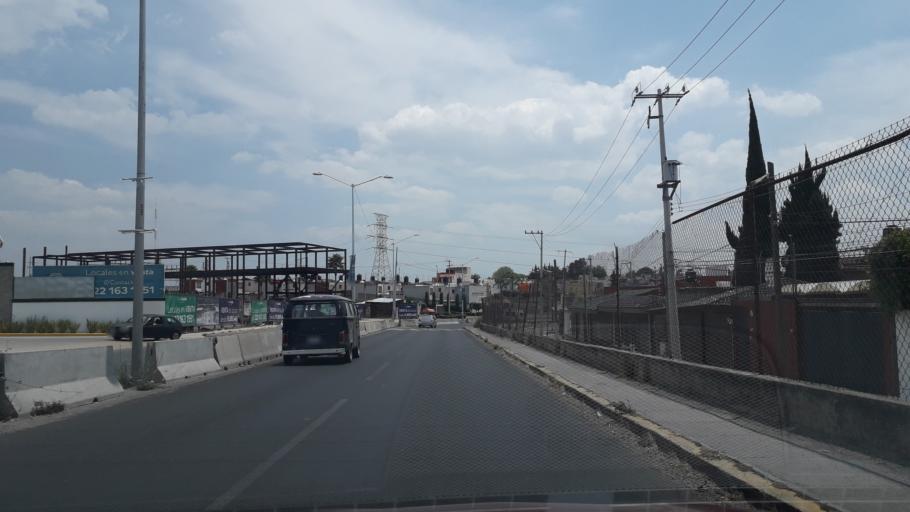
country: MX
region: Puebla
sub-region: Puebla
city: Galaxia la Calera
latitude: 19.0017
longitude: -98.1811
